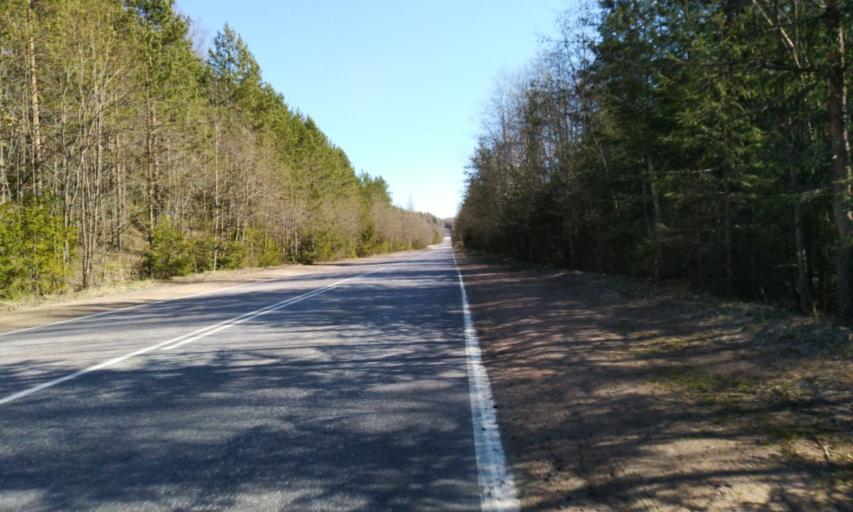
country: RU
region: Leningrad
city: Garbolovo
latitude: 60.3783
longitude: 30.4607
